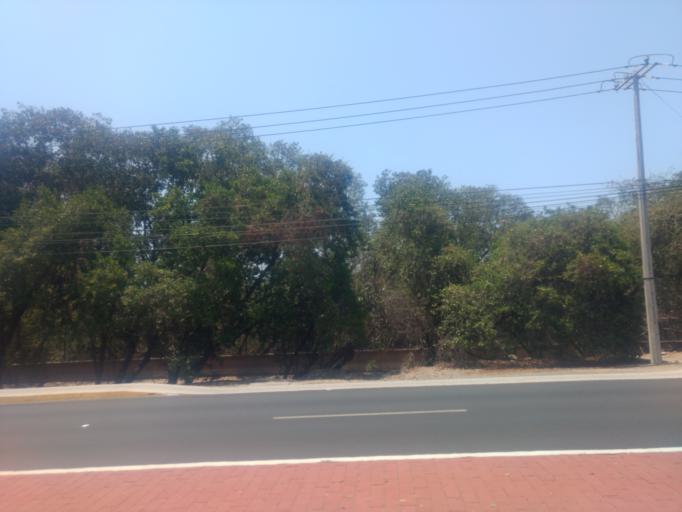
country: MX
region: Colima
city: Tapeixtles
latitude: 19.0857
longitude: -104.3053
